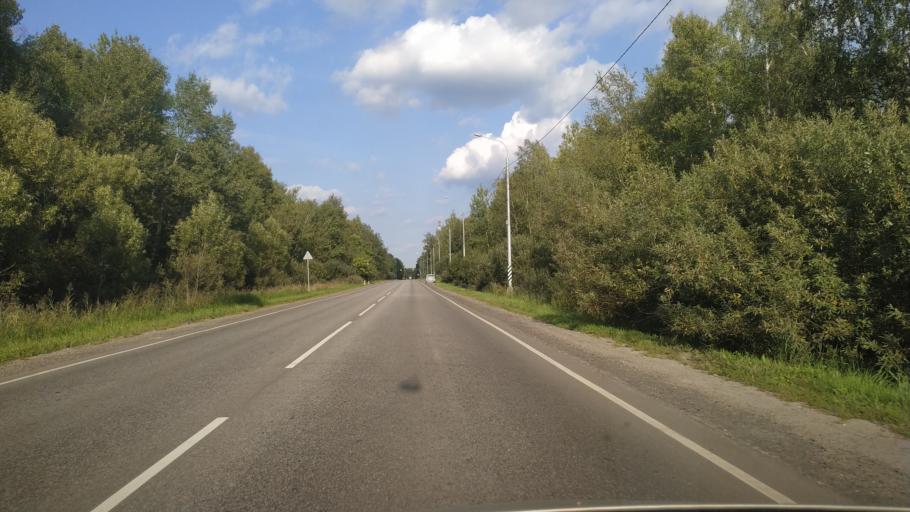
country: RU
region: Moskovskaya
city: Likino-Dulevo
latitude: 55.7274
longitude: 38.9802
